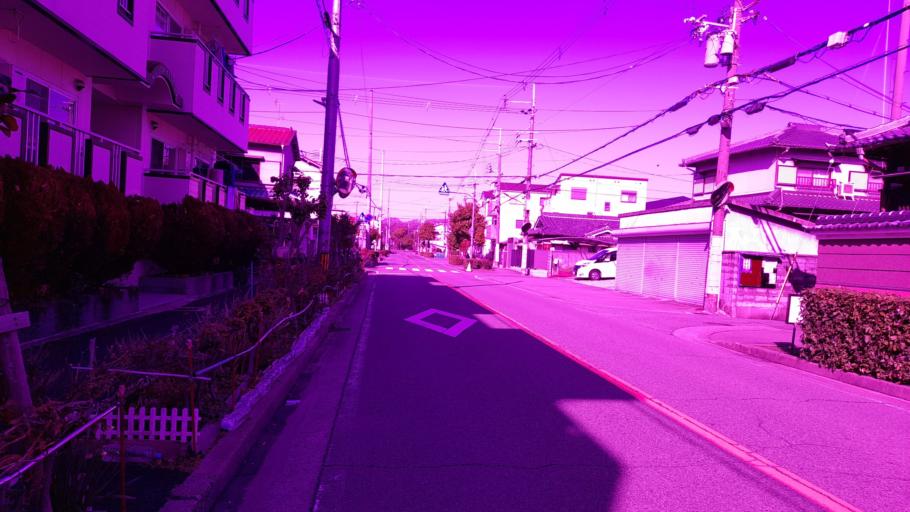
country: JP
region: Osaka
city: Toyonaka
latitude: 34.7623
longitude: 135.4479
